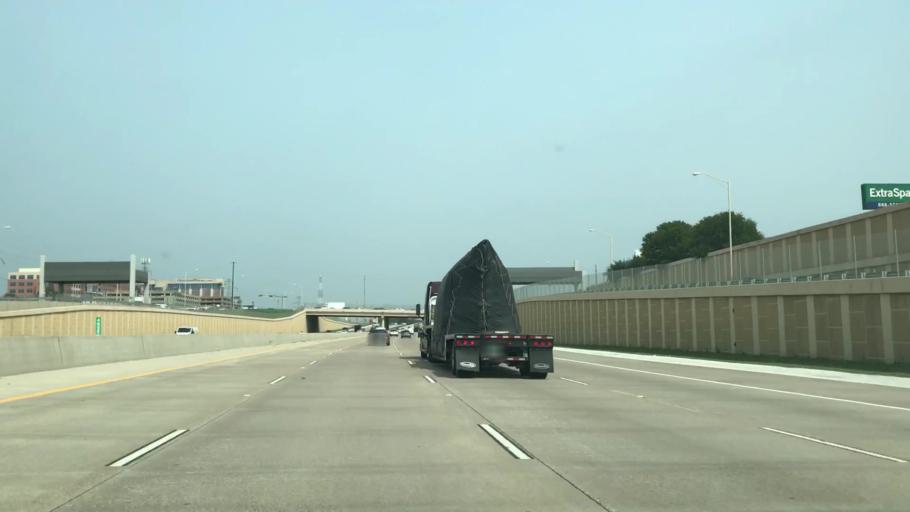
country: US
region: Texas
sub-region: Dallas County
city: Addison
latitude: 33.0124
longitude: -96.7997
